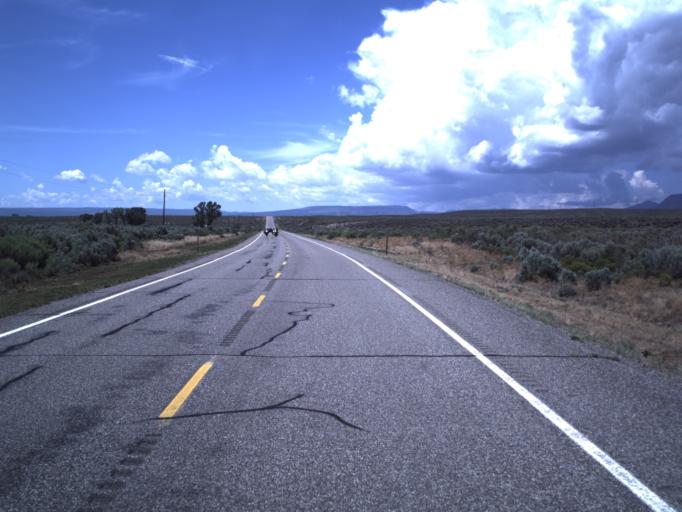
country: US
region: Utah
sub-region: Garfield County
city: Panguitch
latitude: 38.0037
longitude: -112.3821
